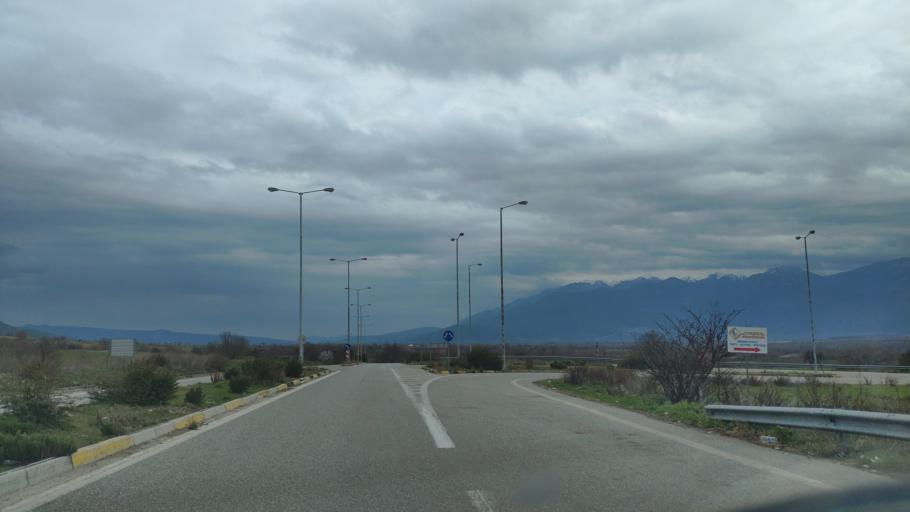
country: GR
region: Central Greece
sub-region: Nomos Fthiotidos
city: Anthili
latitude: 38.7128
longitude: 22.4607
